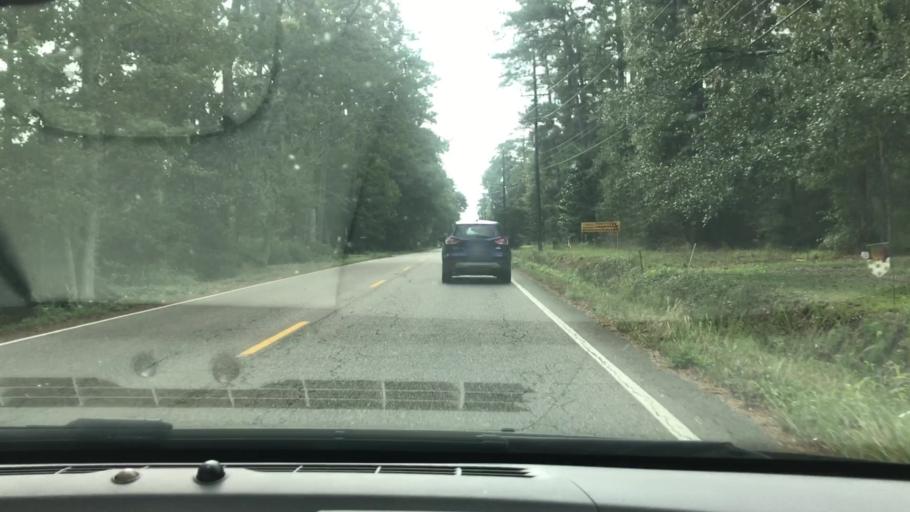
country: US
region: Louisiana
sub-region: Saint Tammany Parish
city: Abita Springs
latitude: 30.4731
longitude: -90.0408
